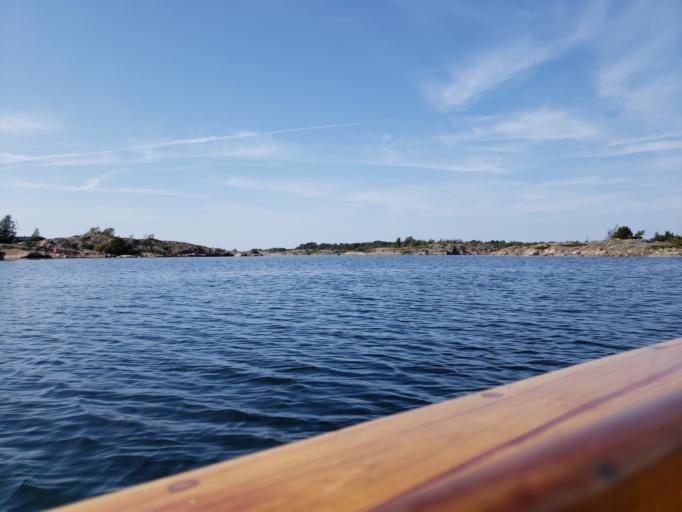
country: FI
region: Varsinais-Suomi
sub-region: Aboland-Turunmaa
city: Dragsfjaerd
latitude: 59.8465
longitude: 22.2063
